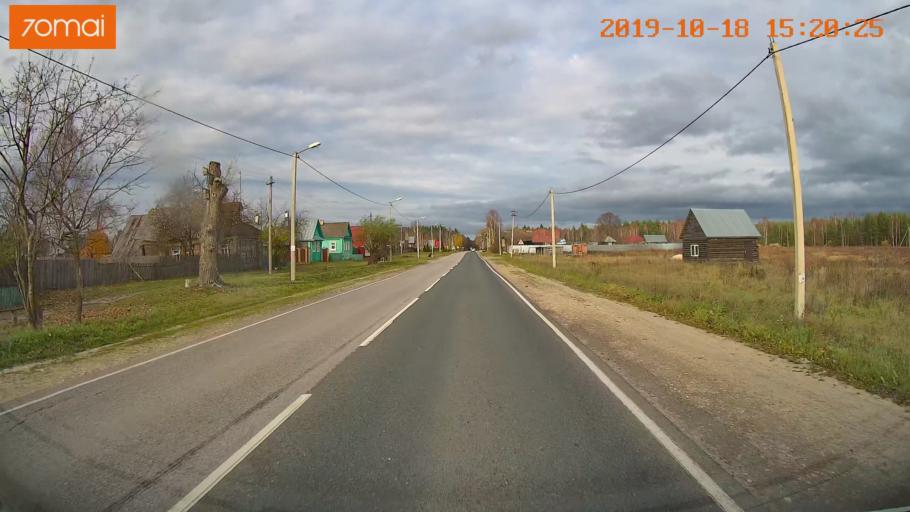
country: RU
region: Vladimir
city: Anopino
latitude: 55.6867
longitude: 40.7446
